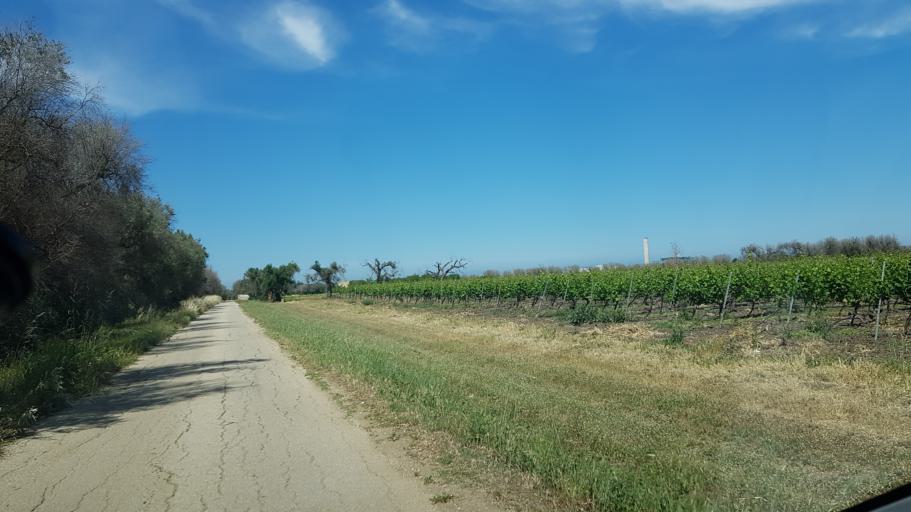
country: IT
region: Apulia
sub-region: Provincia di Brindisi
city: Tuturano
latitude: 40.5390
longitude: 17.9973
